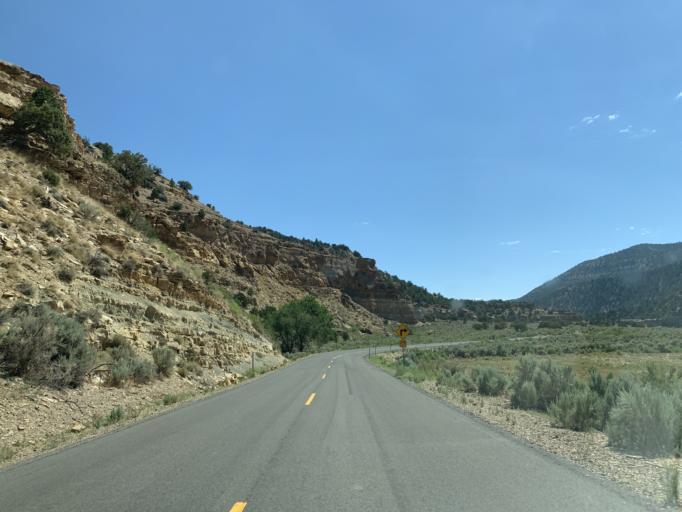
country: US
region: Utah
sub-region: Carbon County
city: East Carbon City
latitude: 39.7784
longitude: -110.4413
